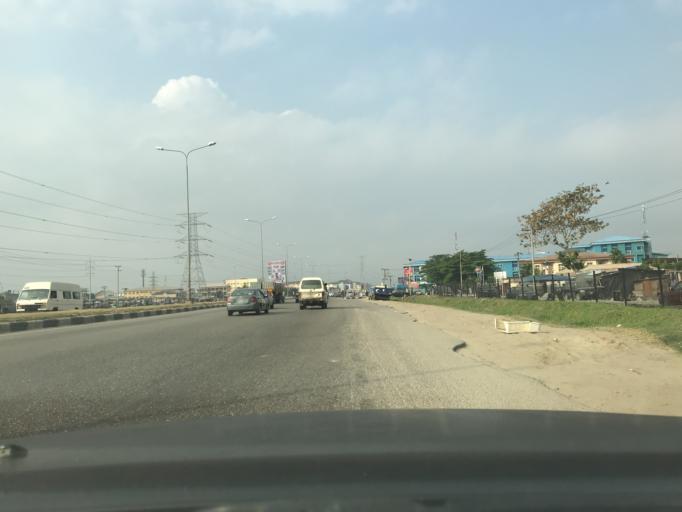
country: NG
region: Lagos
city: Ikoyi
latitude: 6.4404
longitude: 3.5282
